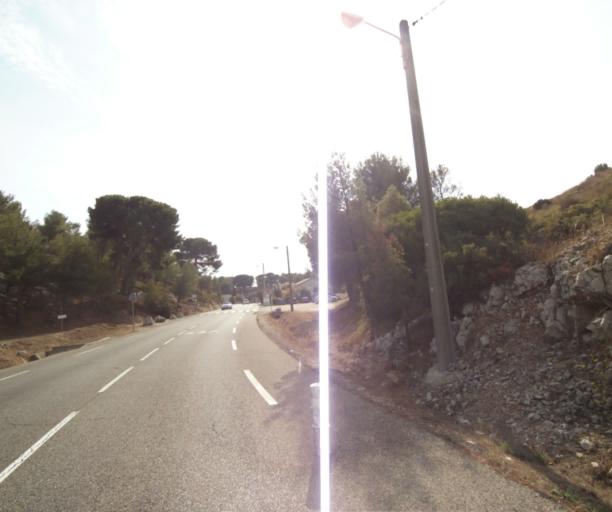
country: FR
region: Provence-Alpes-Cote d'Azur
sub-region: Departement des Bouches-du-Rhone
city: Sausset-les-Pins
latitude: 43.3360
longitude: 5.1088
